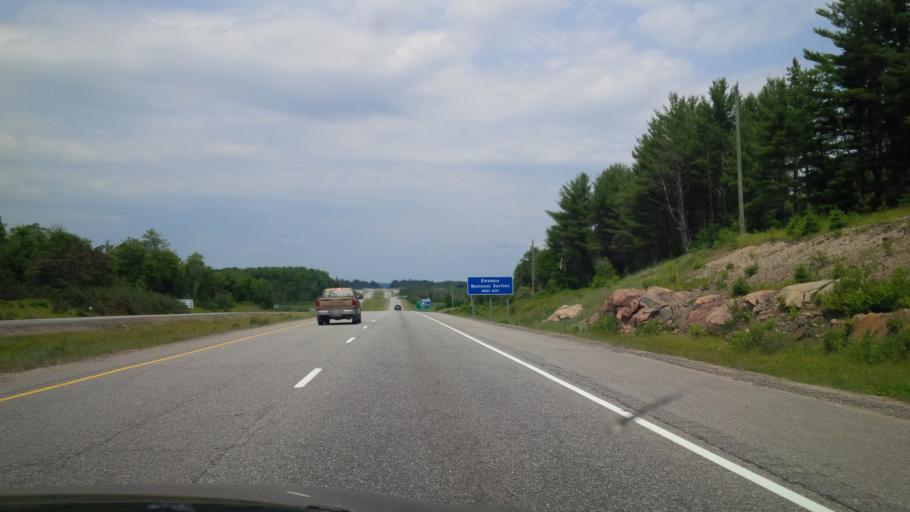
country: CA
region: Ontario
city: Huntsville
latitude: 45.4971
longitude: -79.2933
